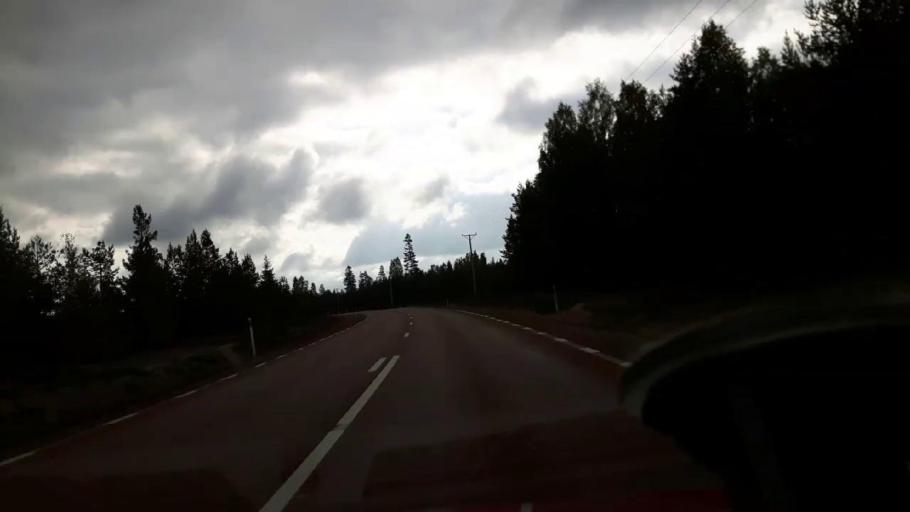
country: SE
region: Gaevleborg
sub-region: Soderhamns Kommun
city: Ljusne
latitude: 61.1146
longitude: 16.9348
